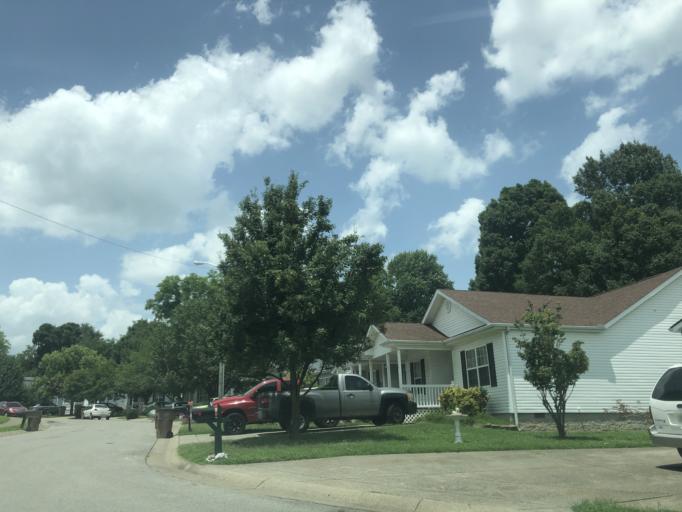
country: US
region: Tennessee
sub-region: Williamson County
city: Nolensville
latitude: 36.0505
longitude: -86.6777
